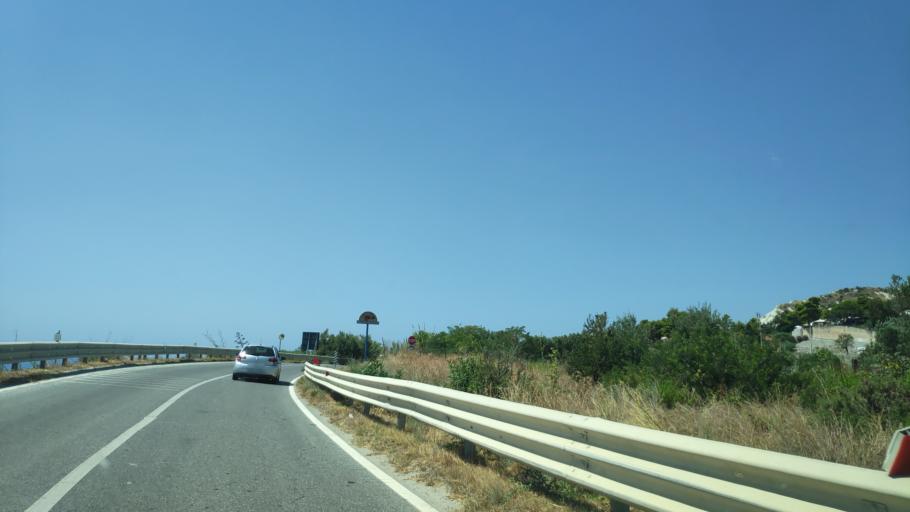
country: IT
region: Calabria
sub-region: Provincia di Reggio Calabria
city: Palizzi Marina
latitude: 37.9210
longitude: 16.0117
